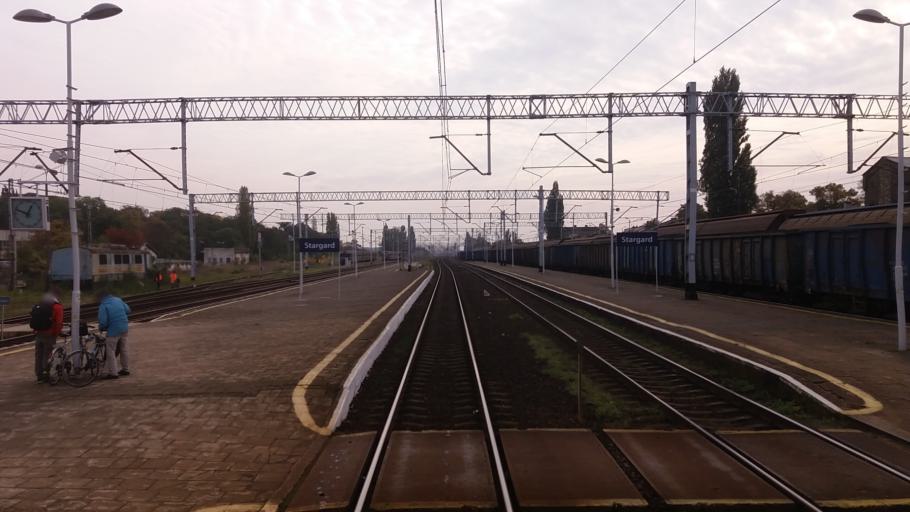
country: PL
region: West Pomeranian Voivodeship
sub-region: Powiat stargardzki
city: Stargard Szczecinski
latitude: 53.3386
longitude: 15.0319
